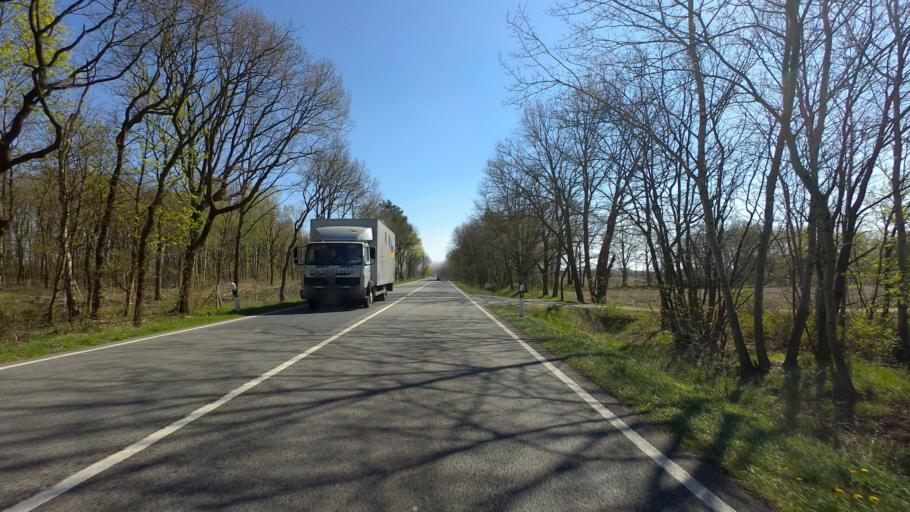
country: DE
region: Saxony-Anhalt
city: Pretzier
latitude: 52.7721
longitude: 11.2358
